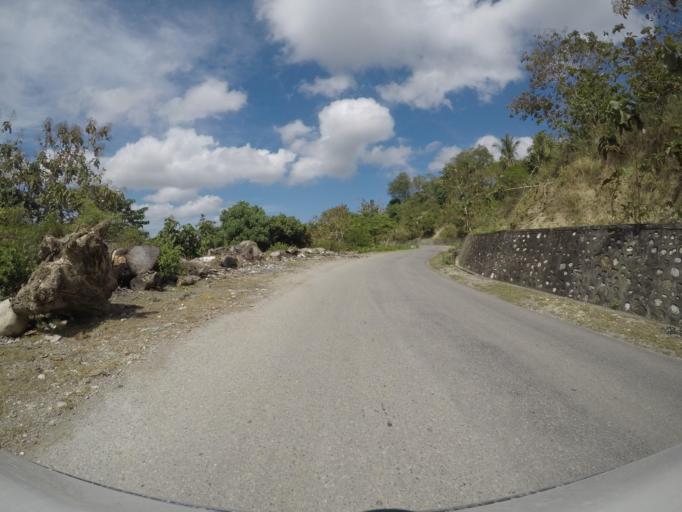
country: TL
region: Viqueque
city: Viqueque
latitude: -8.8736
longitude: 126.3590
